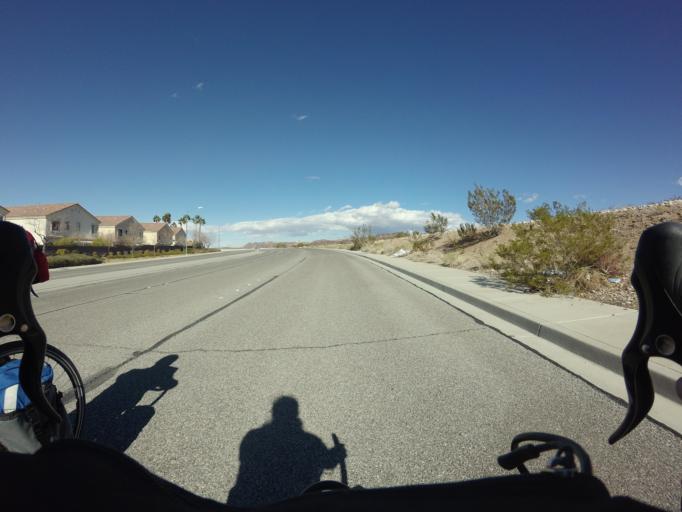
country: US
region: Nevada
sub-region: Clark County
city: Henderson
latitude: 35.9905
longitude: -114.9235
